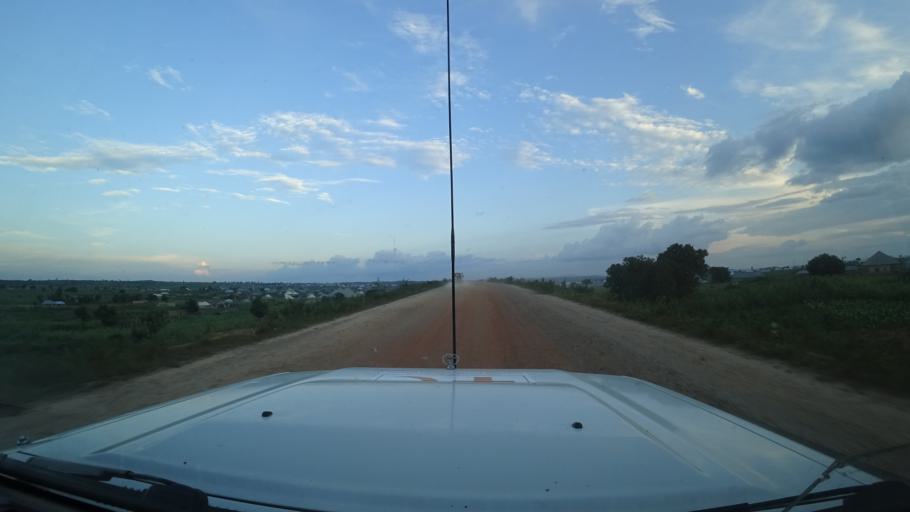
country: NG
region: Niger
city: Minna
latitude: 9.6523
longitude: 6.5772
